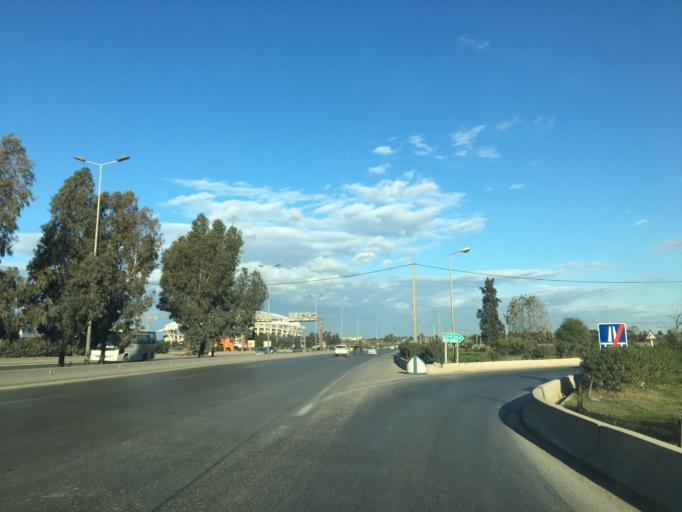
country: DZ
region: Tipaza
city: Baraki
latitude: 36.6874
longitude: 3.1152
